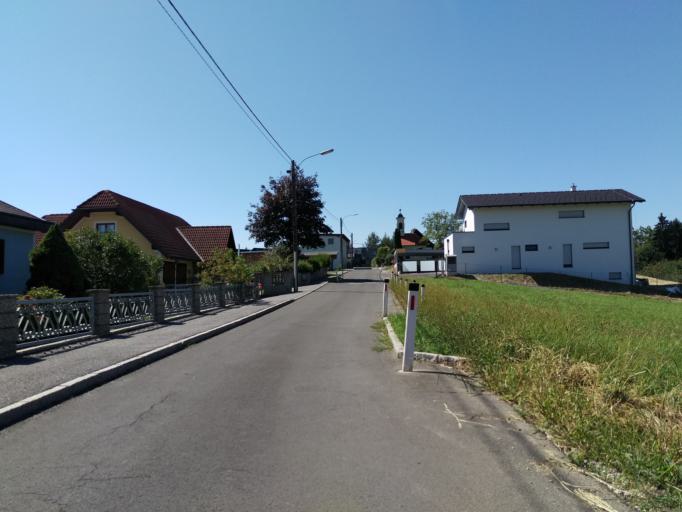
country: AT
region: Styria
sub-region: Politischer Bezirk Graz-Umgebung
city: Hart bei Graz
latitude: 47.0755
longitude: 15.5402
